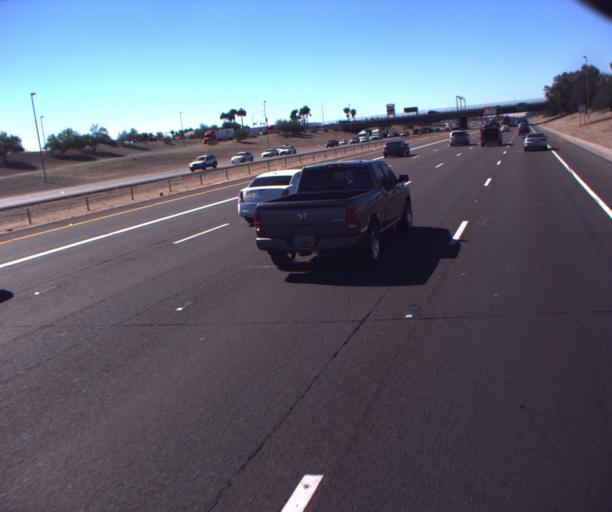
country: US
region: Arizona
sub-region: Maricopa County
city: Tolleson
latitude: 33.4630
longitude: -112.2004
